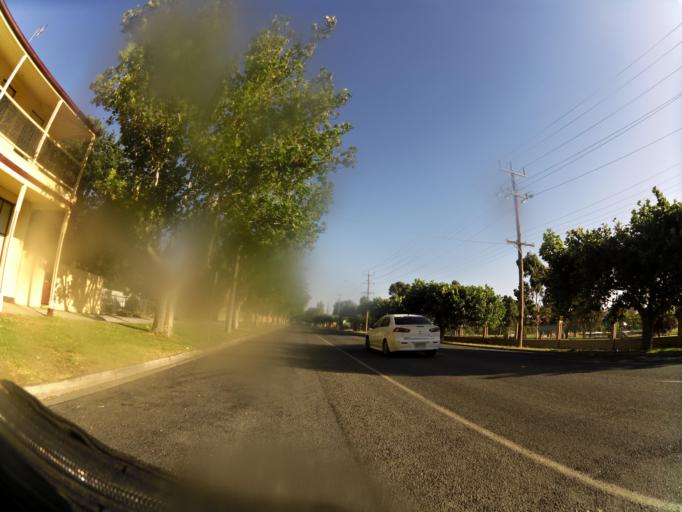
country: AU
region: Victoria
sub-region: Murrindindi
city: Kinglake West
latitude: -37.0208
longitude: 145.1303
